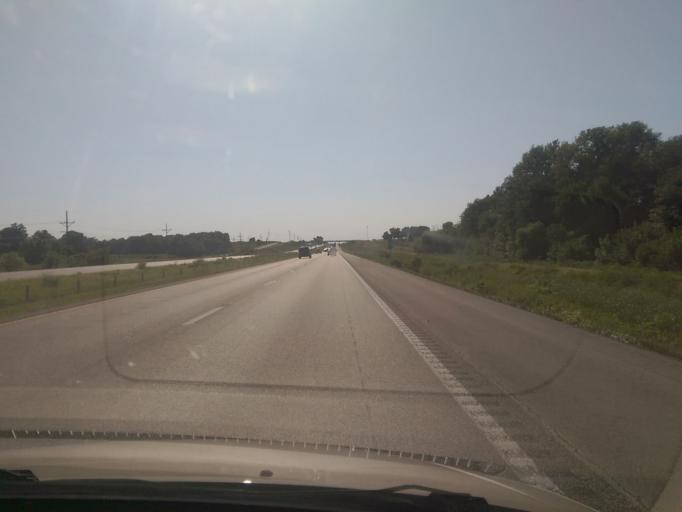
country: US
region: Missouri
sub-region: Saline County
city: Sweet Springs
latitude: 38.9784
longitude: -93.4497
